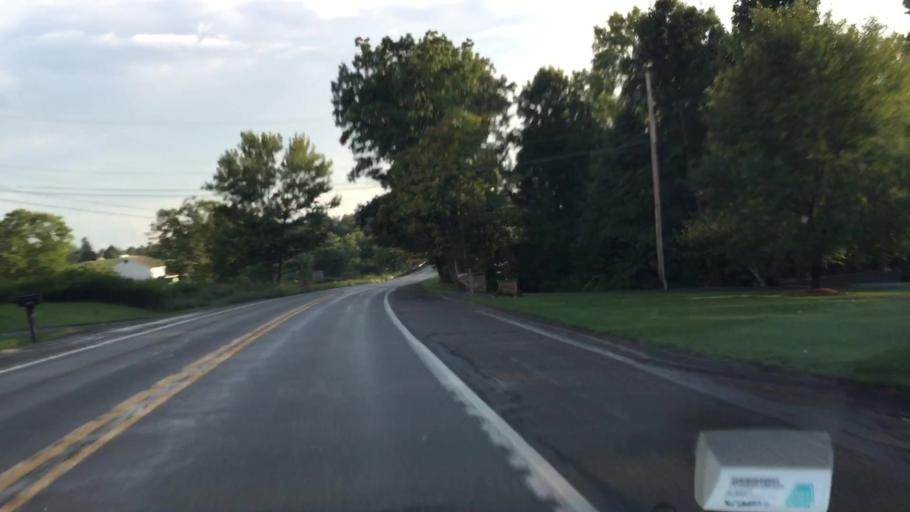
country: US
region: Pennsylvania
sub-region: Butler County
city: Meridian
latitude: 40.8147
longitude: -80.0109
